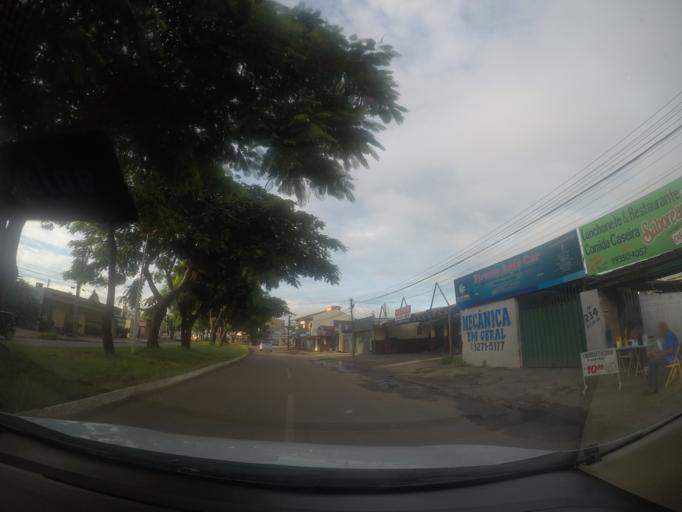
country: BR
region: Goias
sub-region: Goiania
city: Goiania
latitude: -16.6826
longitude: -49.3107
